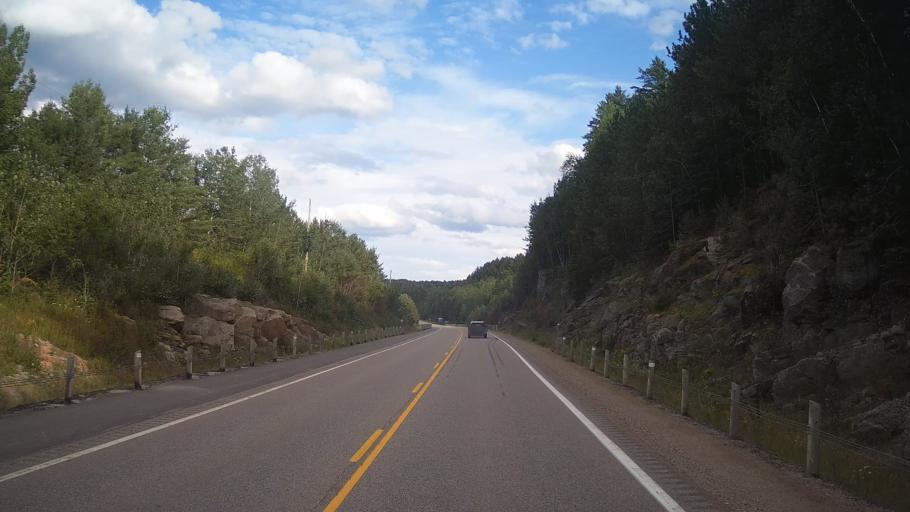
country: CA
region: Ontario
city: Mattawa
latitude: 46.2511
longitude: -78.3186
